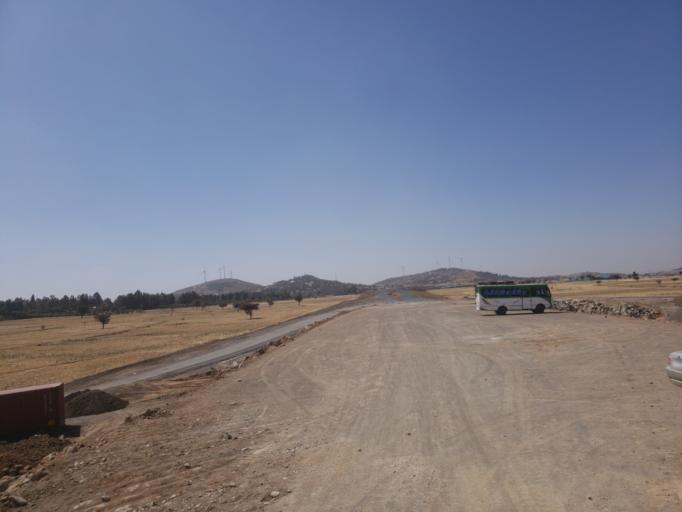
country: ET
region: Oromiya
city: Mojo
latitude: 8.5792
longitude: 39.1730
